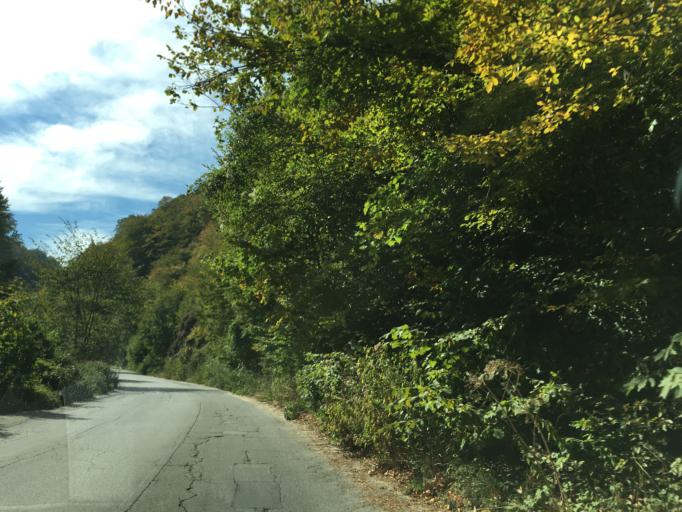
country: BG
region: Pazardzhik
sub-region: Obshtina Batak
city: Batak
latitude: 41.9830
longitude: 24.2467
